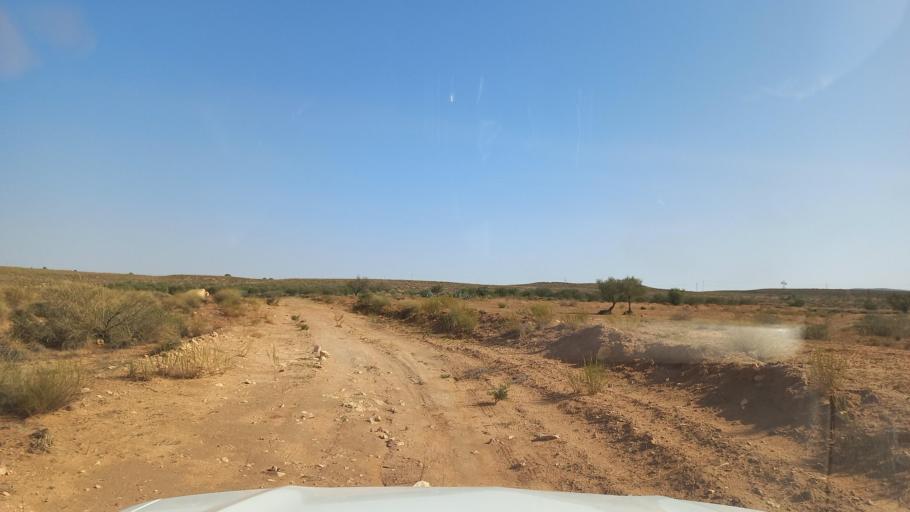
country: TN
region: Al Qasrayn
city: Kasserine
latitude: 35.2040
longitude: 8.9728
